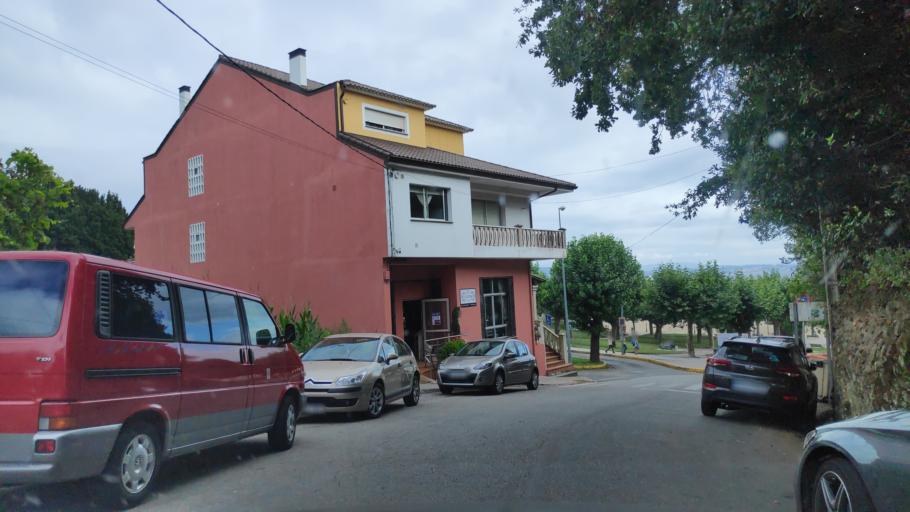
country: ES
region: Galicia
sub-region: Provincia da Coruna
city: Rianxo
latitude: 42.6462
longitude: -8.8136
